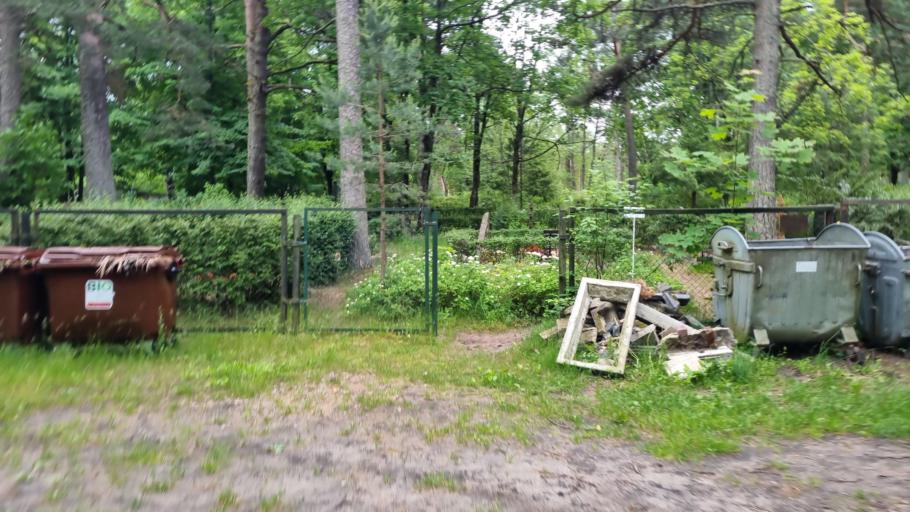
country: LV
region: Riga
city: Daugavgriva
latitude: 57.0218
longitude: 24.0257
